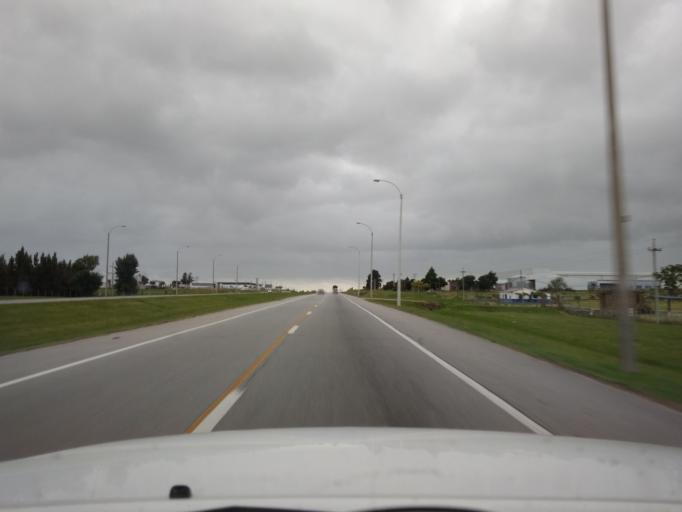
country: UY
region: Canelones
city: Las Piedras
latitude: -34.6976
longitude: -56.2388
